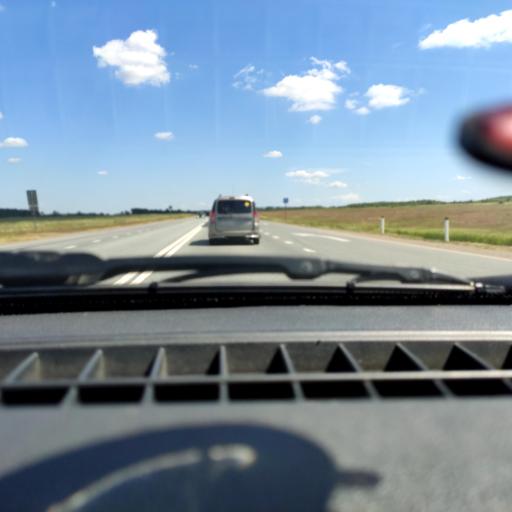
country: RU
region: Bashkortostan
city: Kudeyevskiy
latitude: 54.8172
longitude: 56.8061
